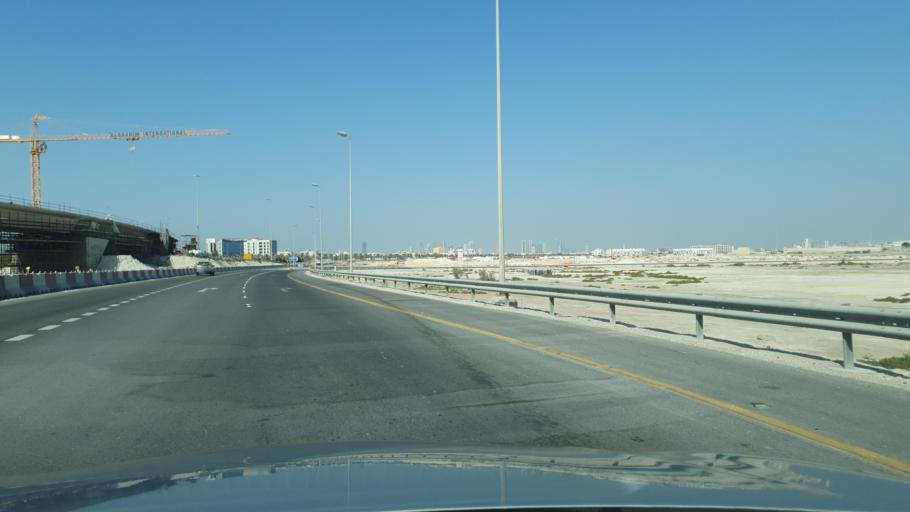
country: BH
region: Northern
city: Madinat `Isa
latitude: 26.1812
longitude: 50.5033
